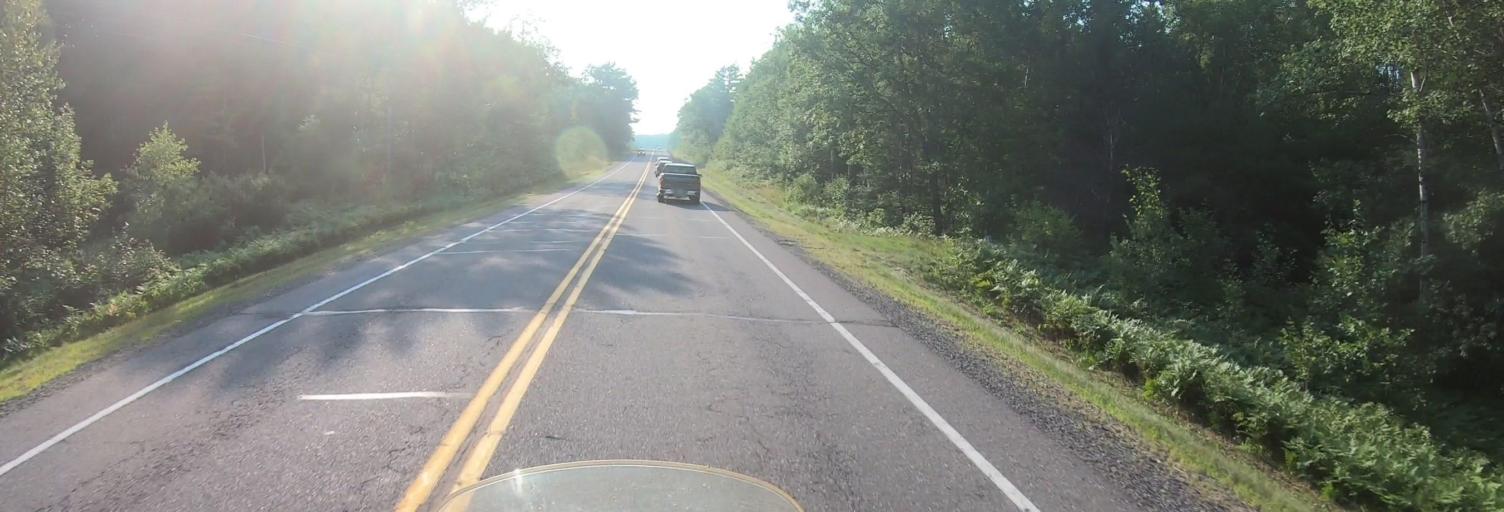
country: US
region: Wisconsin
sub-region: Sawyer County
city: Little Round Lake
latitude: 46.0645
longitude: -91.1606
